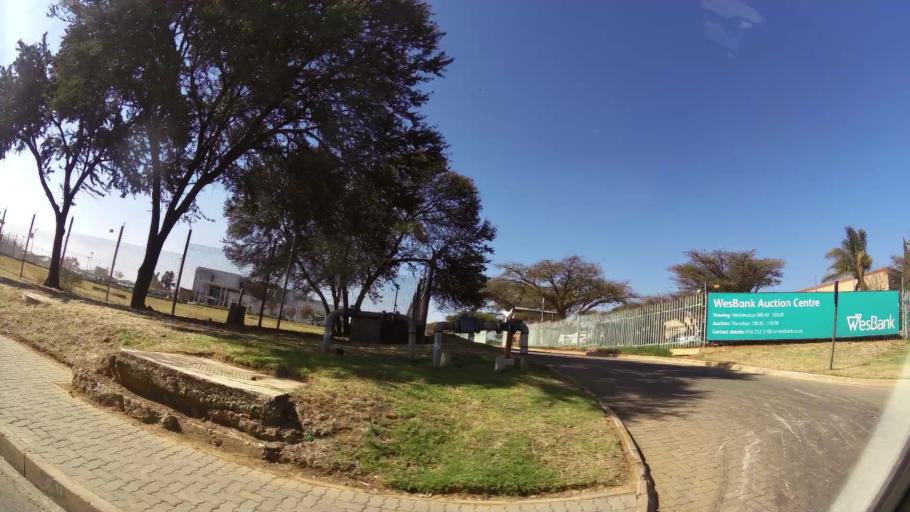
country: ZA
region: Gauteng
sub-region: City of Johannesburg Metropolitan Municipality
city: Midrand
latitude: -25.9584
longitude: 28.1299
